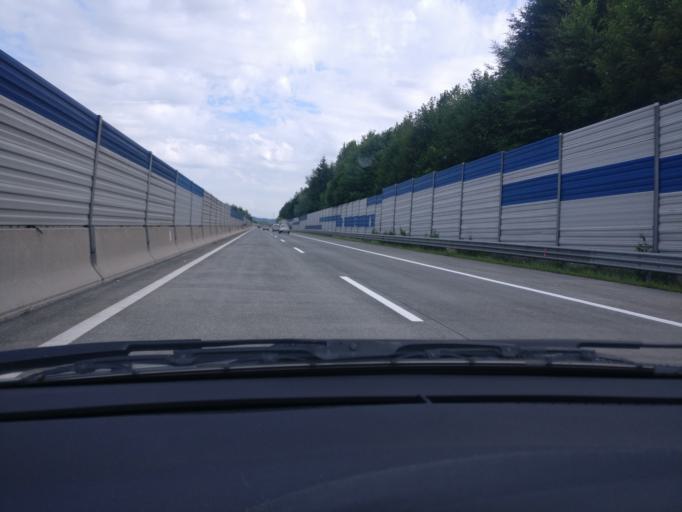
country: AT
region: Upper Austria
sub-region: Politischer Bezirk Vocklabruck
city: Oberwang
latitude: 47.8739
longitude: 13.4350
